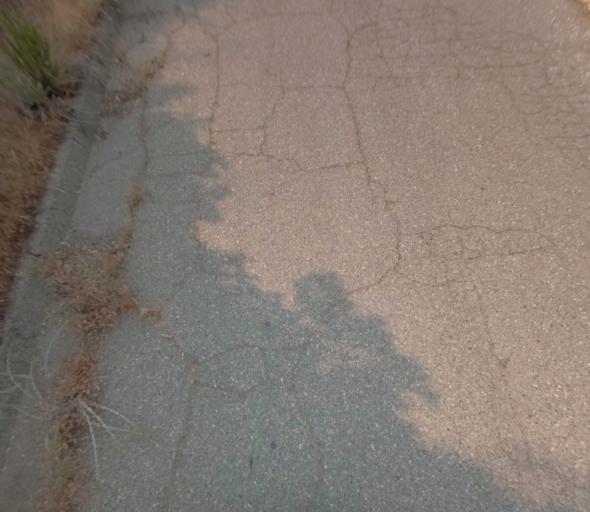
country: US
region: California
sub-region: Madera County
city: Oakhurst
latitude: 37.3062
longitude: -119.6265
